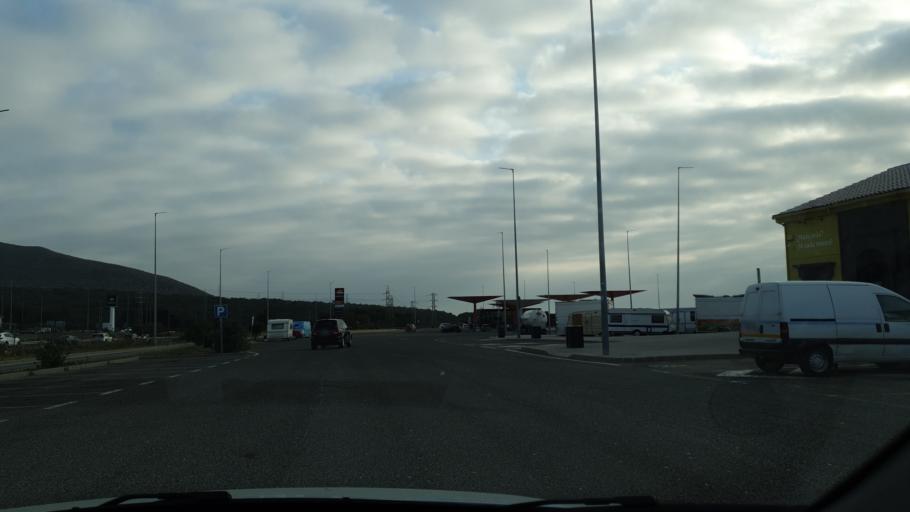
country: ES
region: Andalusia
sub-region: Provincia de Malaga
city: Torremolinos
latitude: 36.6115
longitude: -4.5289
